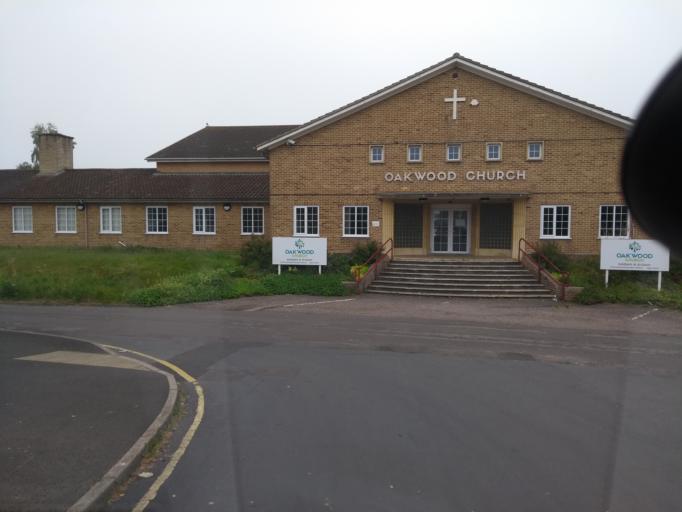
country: GB
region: England
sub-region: Somerset
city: Taunton
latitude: 51.0260
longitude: -3.0957
